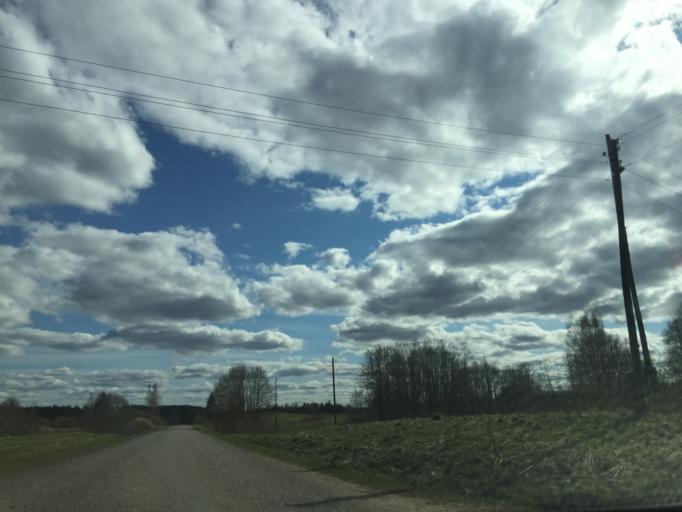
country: LV
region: Rezekne
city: Rezekne
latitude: 56.6132
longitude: 27.3176
